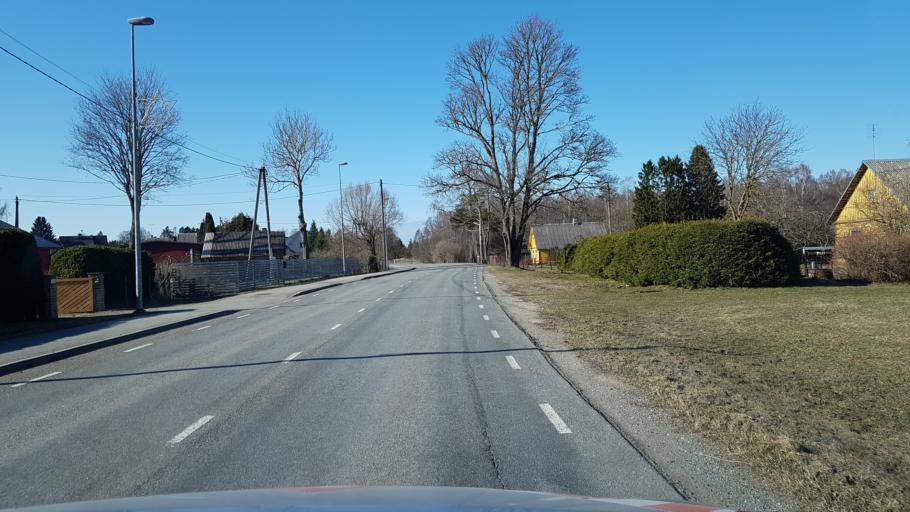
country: EE
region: Laeaene-Virumaa
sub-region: Haljala vald
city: Haljala
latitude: 59.4376
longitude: 26.2635
